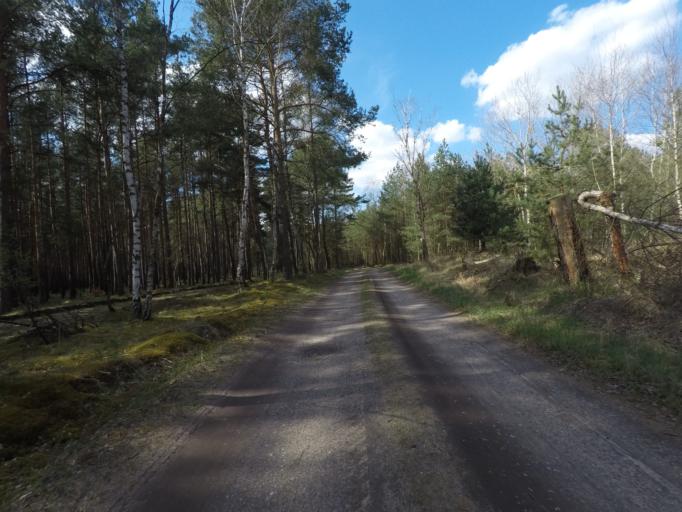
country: DE
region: Brandenburg
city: Melchow
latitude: 52.8182
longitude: 13.6940
